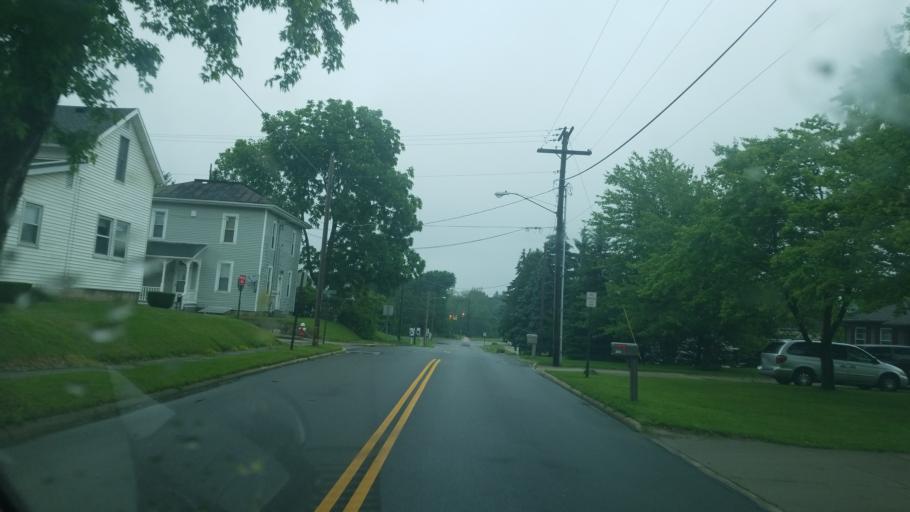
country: US
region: Ohio
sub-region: Crawford County
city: Bucyrus
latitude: 40.8095
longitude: -82.9592
